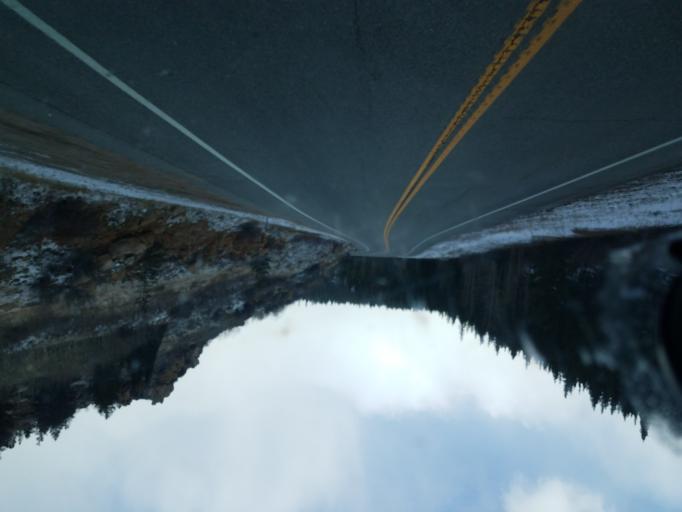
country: US
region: Colorado
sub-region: Clear Creek County
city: Georgetown
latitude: 39.4435
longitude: -105.7424
